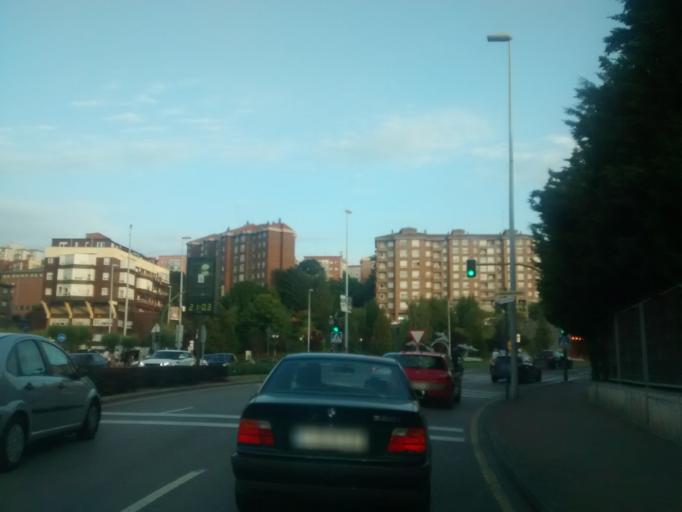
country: ES
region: Cantabria
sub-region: Provincia de Cantabria
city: Santander
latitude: 43.4731
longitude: -3.7934
